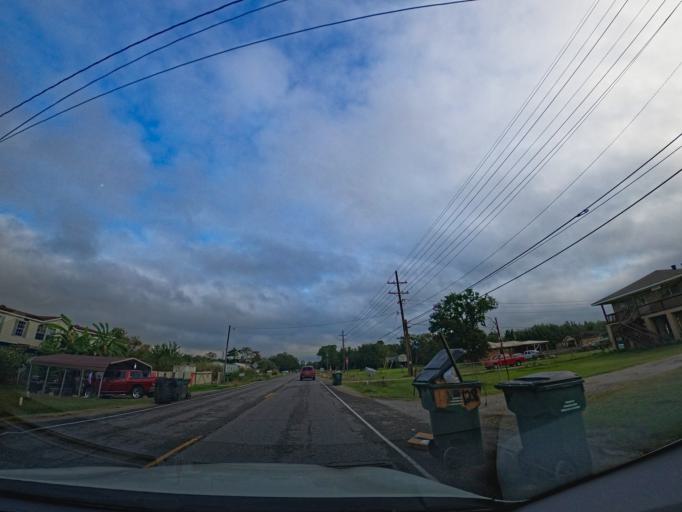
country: US
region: Louisiana
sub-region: Terrebonne Parish
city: Dulac
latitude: 29.4740
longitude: -90.7010
